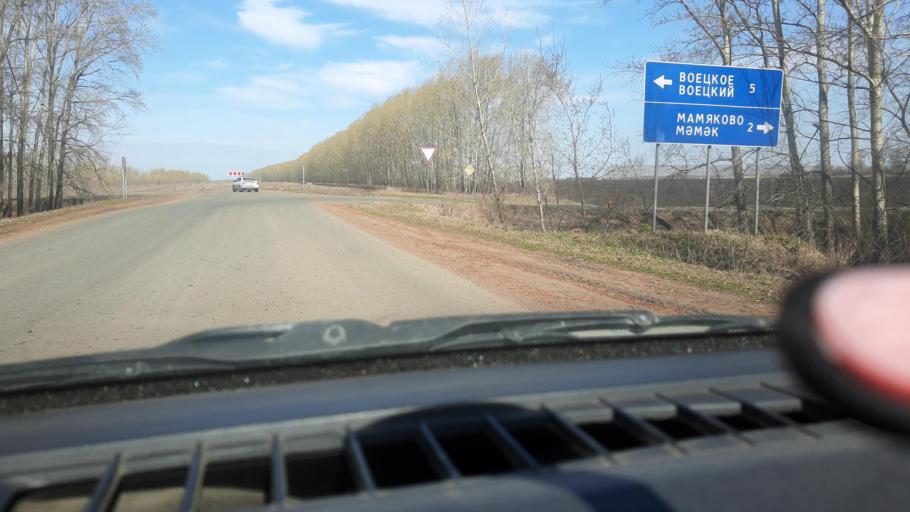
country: RU
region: Bashkortostan
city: Asanovo
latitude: 54.9711
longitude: 55.5384
